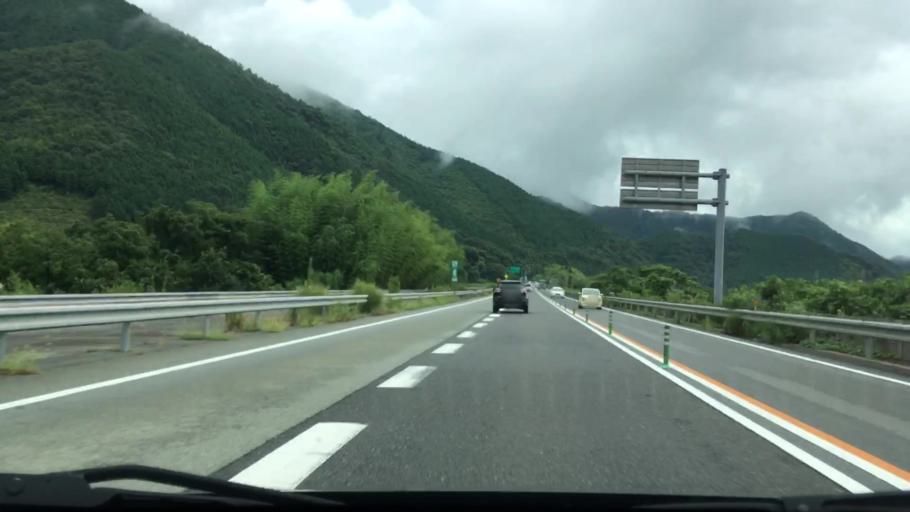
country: JP
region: Hyogo
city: Nishiwaki
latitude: 35.0472
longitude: 134.7653
